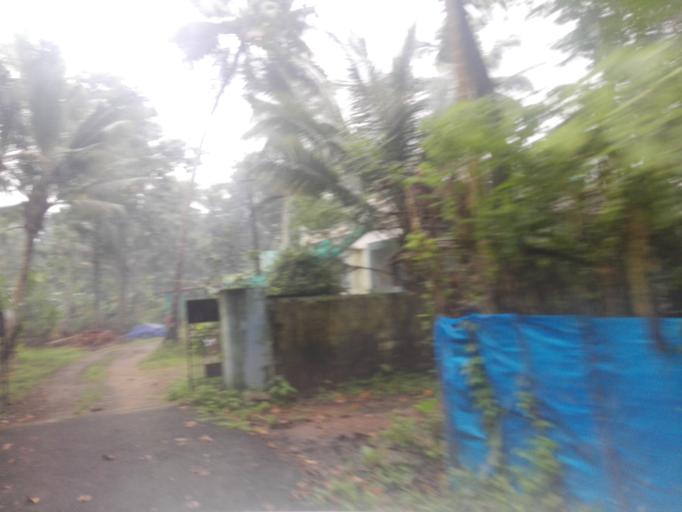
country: IN
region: Kerala
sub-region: Alappuzha
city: Arukutti
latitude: 9.8285
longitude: 76.3899
